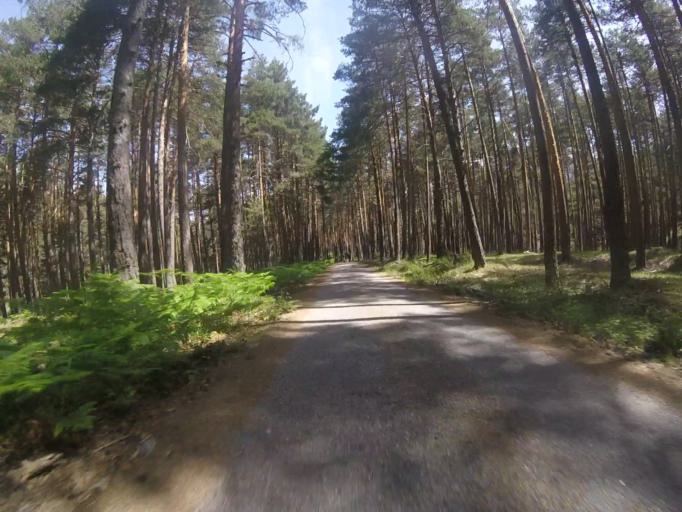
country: ES
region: Madrid
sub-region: Provincia de Madrid
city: Cercedilla
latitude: 40.8170
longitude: -4.0291
